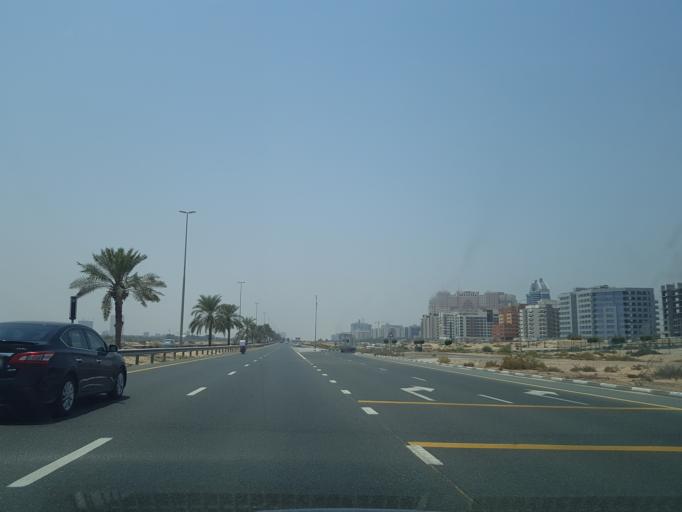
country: AE
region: Ash Shariqah
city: Sharjah
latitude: 25.1205
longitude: 55.4011
